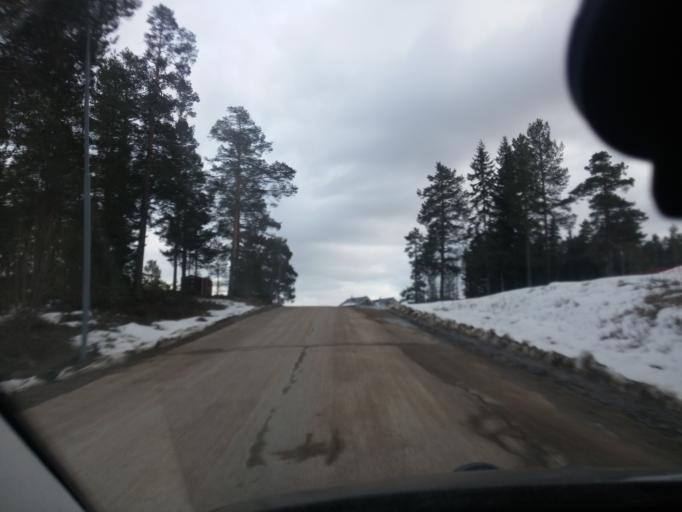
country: SE
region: Gaevleborg
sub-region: Ljusdals Kommun
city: Jaervsoe
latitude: 61.7194
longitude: 16.1575
